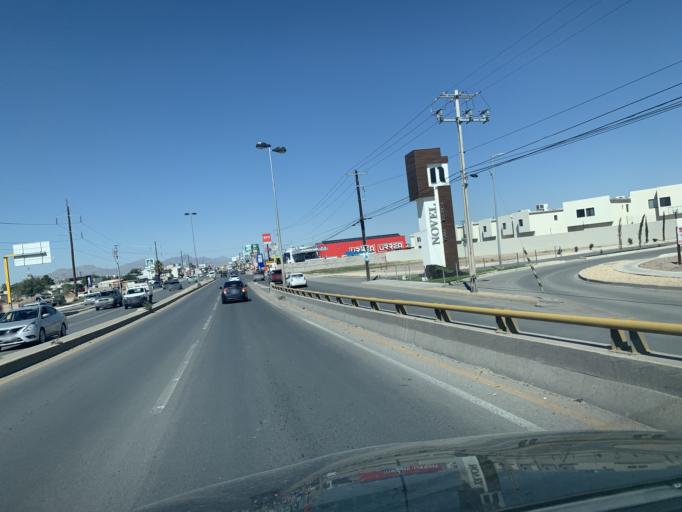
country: US
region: Texas
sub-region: El Paso County
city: Socorro
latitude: 31.6751
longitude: -106.3689
